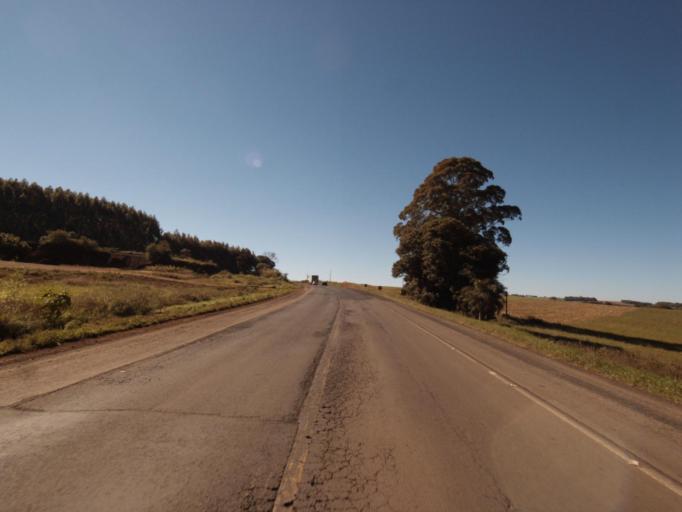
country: BR
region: Rio Grande do Sul
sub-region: Frederico Westphalen
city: Frederico Westphalen
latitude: -26.9171
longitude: -53.1914
